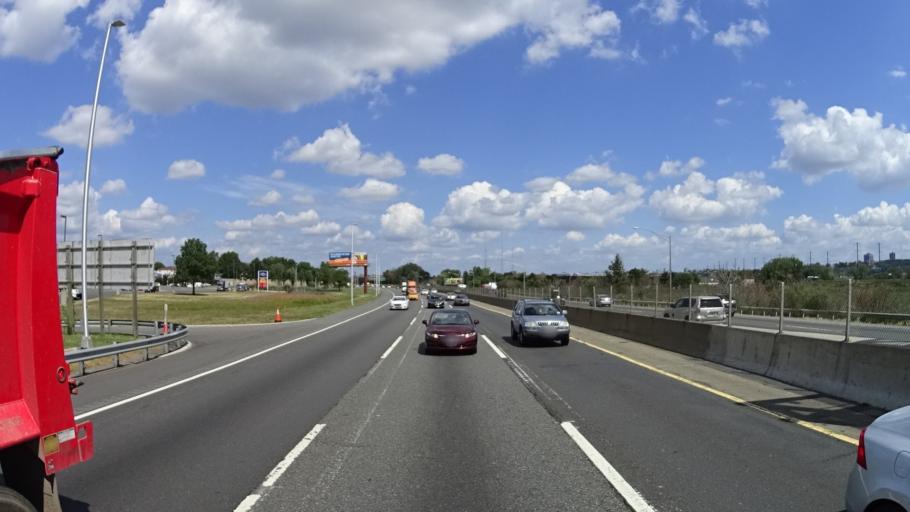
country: US
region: New Jersey
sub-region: Hudson County
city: Secaucus
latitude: 40.7678
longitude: -74.0655
